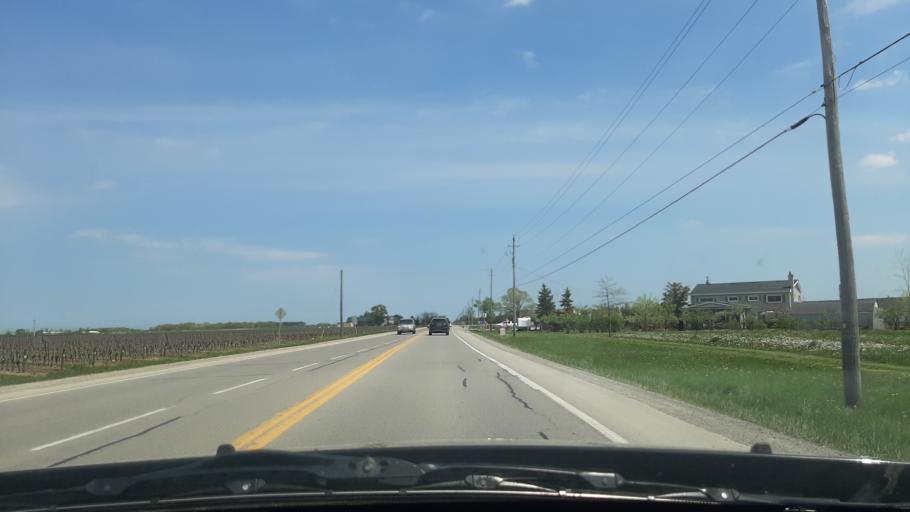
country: CA
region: Ontario
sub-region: Regional Municipality of Niagara
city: St. Catharines
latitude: 43.1864
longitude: -79.1681
